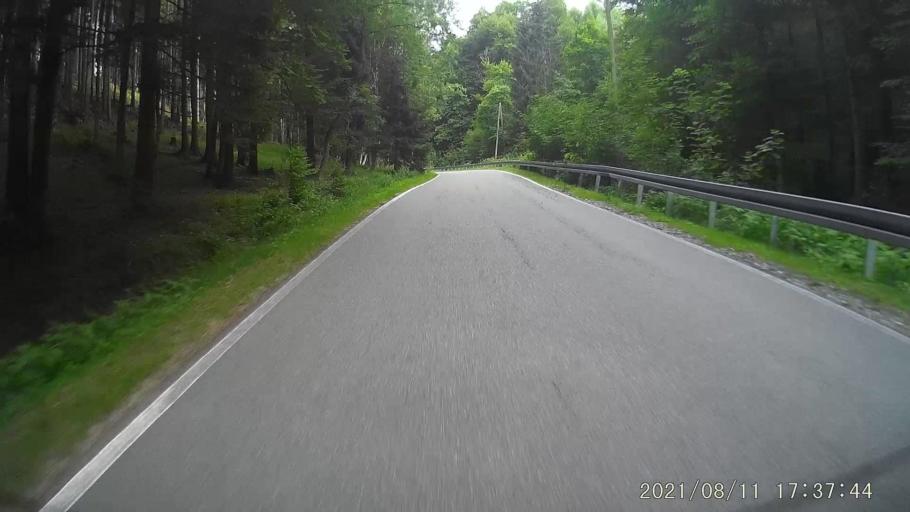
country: PL
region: Lower Silesian Voivodeship
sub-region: Powiat klodzki
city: Duszniki-Zdroj
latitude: 50.3397
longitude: 16.4038
